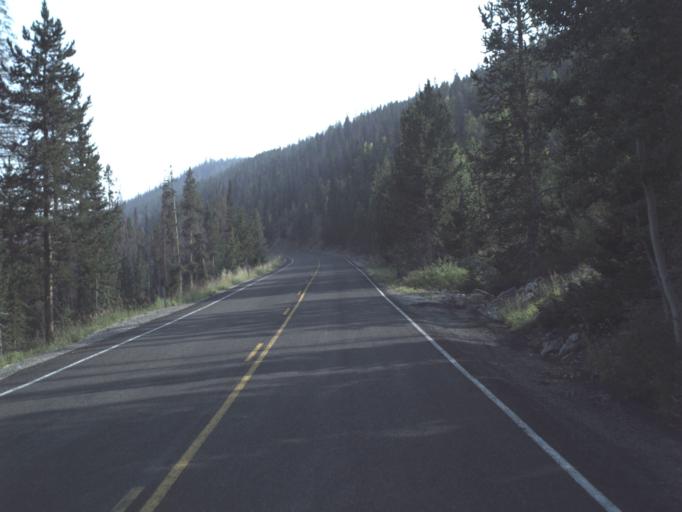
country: US
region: Utah
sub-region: Summit County
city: Kamas
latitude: 40.7878
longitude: -110.8860
